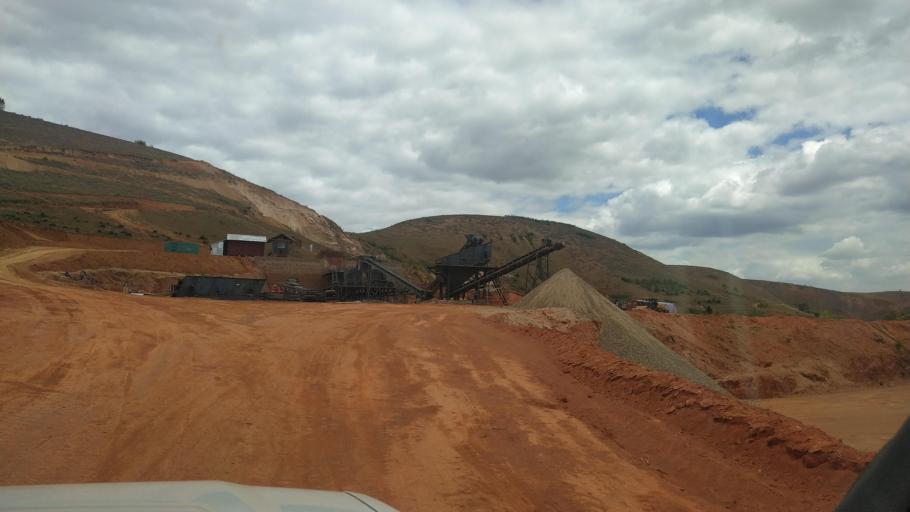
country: MG
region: Alaotra Mangoro
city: Ambatondrazaka
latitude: -17.8835
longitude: 48.2921
